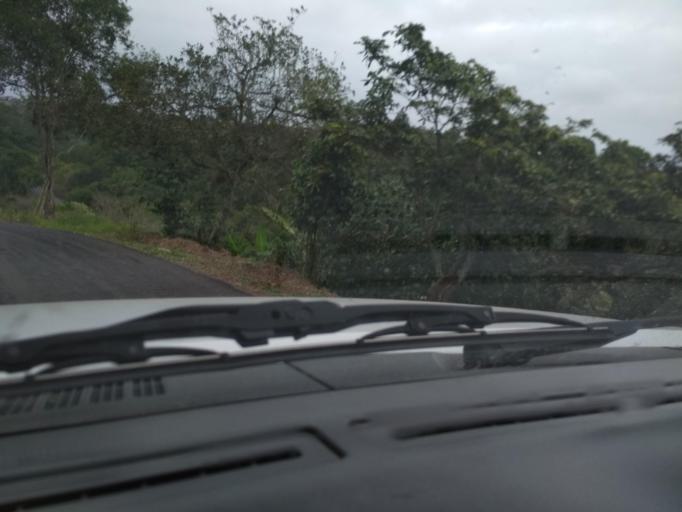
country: MX
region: Veracruz
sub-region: Emiliano Zapata
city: Dos Rios
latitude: 19.5240
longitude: -96.7969
